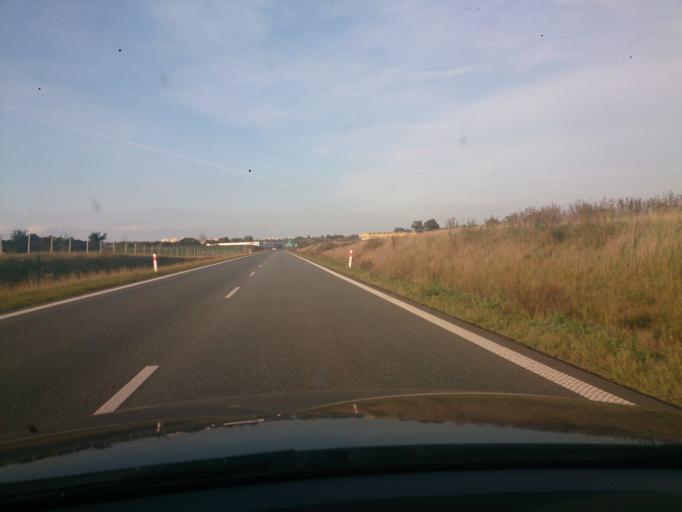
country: PL
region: Kujawsko-Pomorskie
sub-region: Grudziadz
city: Grudziadz
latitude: 53.4338
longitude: 18.7091
